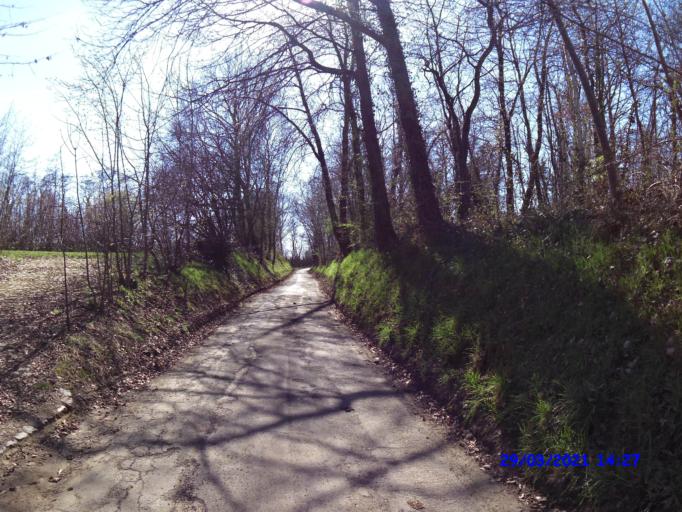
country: BE
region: Flanders
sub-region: Provincie Vlaams-Brabant
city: Bekkevoort
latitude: 50.9306
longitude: 4.9244
